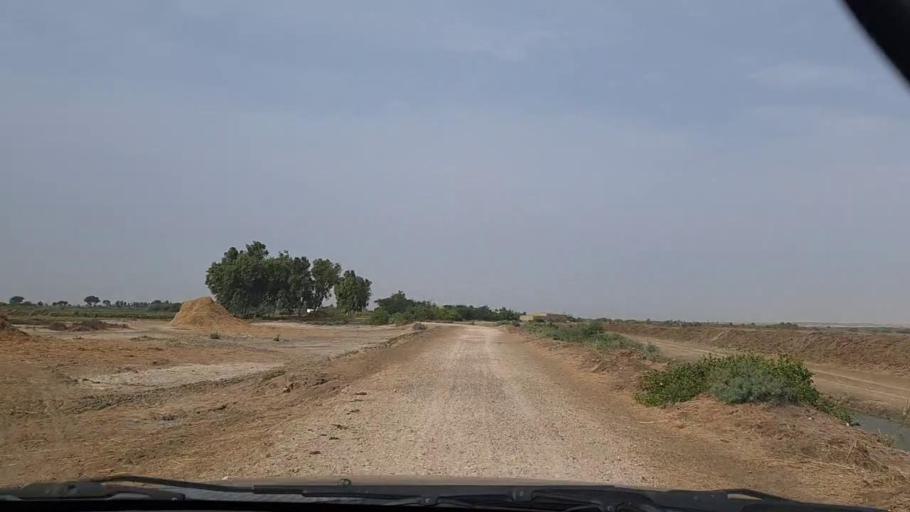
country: PK
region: Sindh
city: Thatta
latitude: 24.5763
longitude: 67.8515
